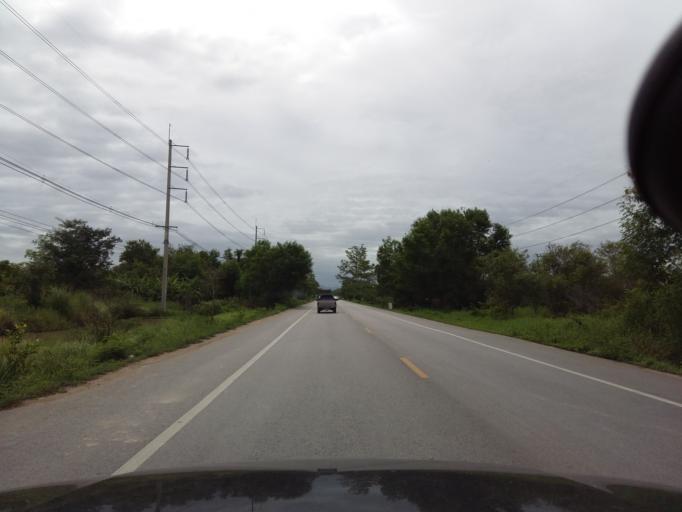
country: TH
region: Chiang Mai
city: Saraphi
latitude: 18.7198
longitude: 98.9753
